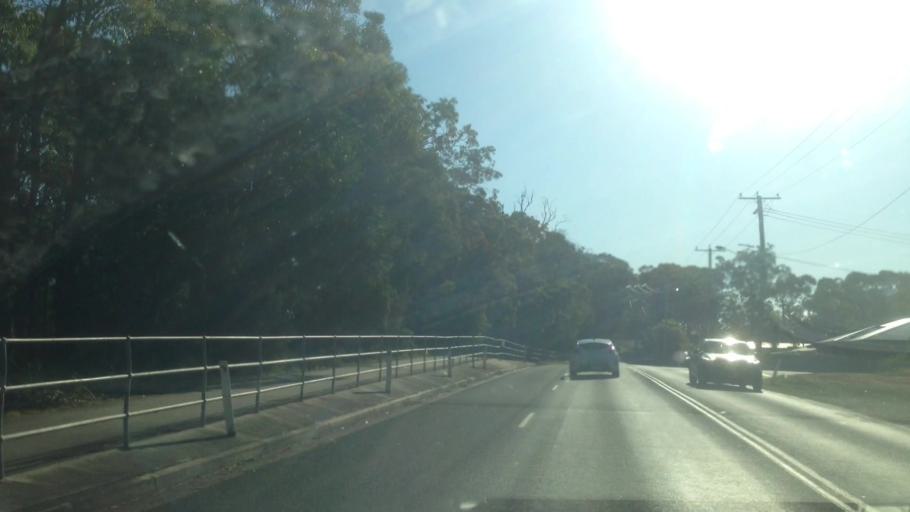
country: AU
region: New South Wales
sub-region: Lake Macquarie Shire
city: Dora Creek
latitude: -33.1120
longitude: 151.5261
